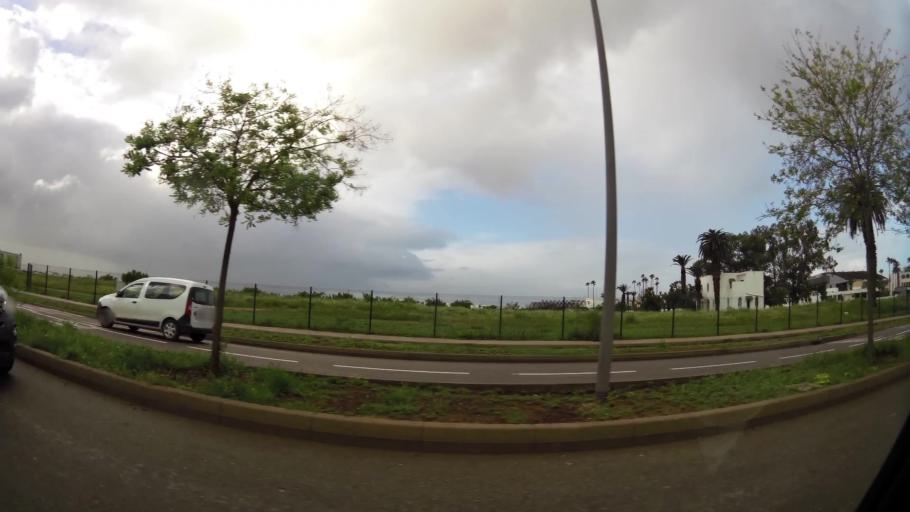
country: MA
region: Grand Casablanca
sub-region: Casablanca
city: Casablanca
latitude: 33.5619
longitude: -7.6632
